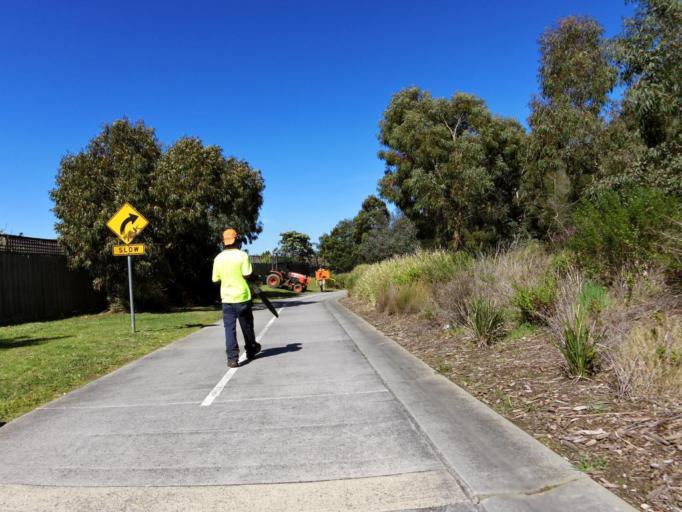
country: AU
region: Victoria
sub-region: Greater Dandenong
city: Noble Park North
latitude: -37.9441
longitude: 145.2069
